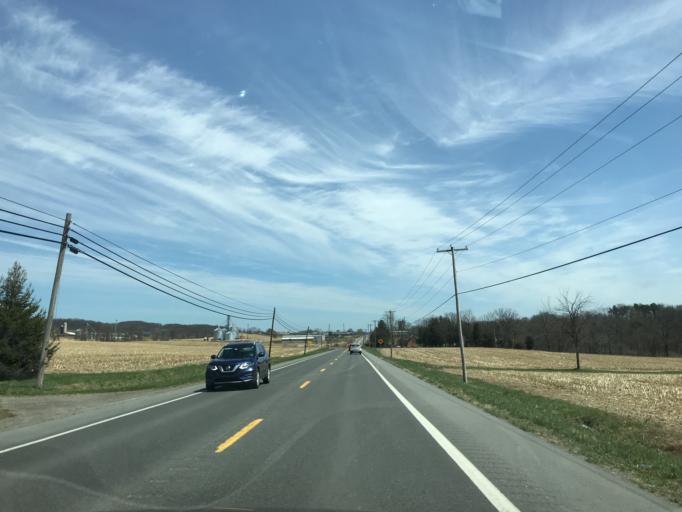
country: US
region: Pennsylvania
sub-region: Snyder County
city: Selinsgrove
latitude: 40.8064
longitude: -76.9295
